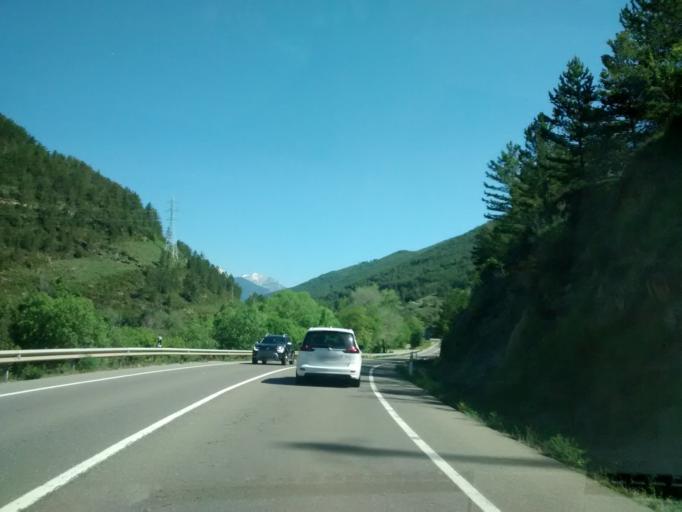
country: ES
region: Aragon
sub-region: Provincia de Huesca
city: Jaca
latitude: 42.5886
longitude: -0.5446
